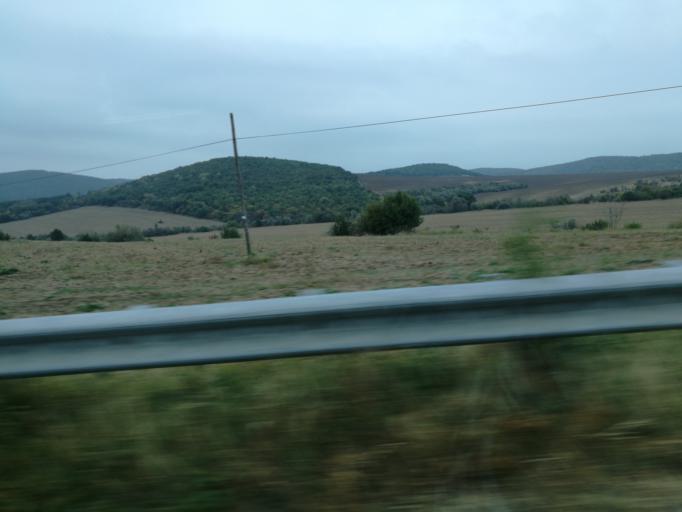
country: RO
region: Tulcea
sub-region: Comuna Horia
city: Horia
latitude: 44.9823
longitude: 28.4476
